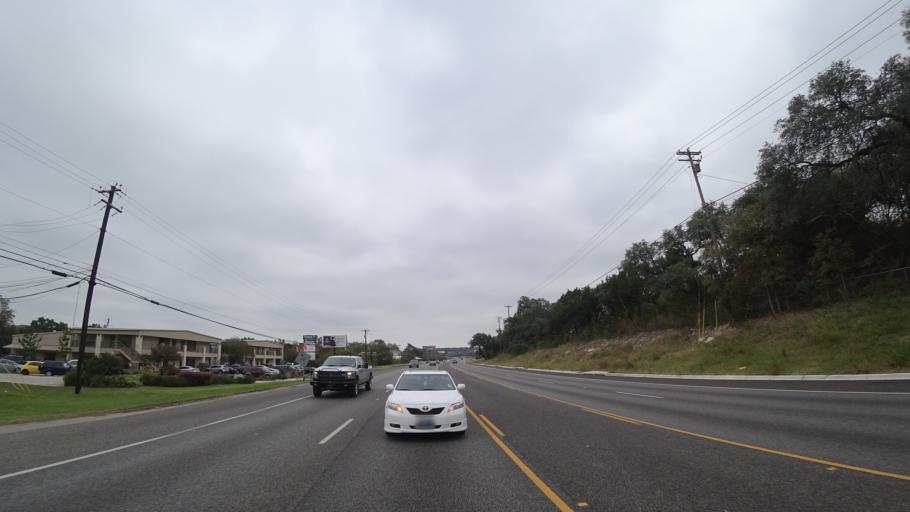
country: US
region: Texas
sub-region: Travis County
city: Barton Creek
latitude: 30.2413
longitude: -97.8814
